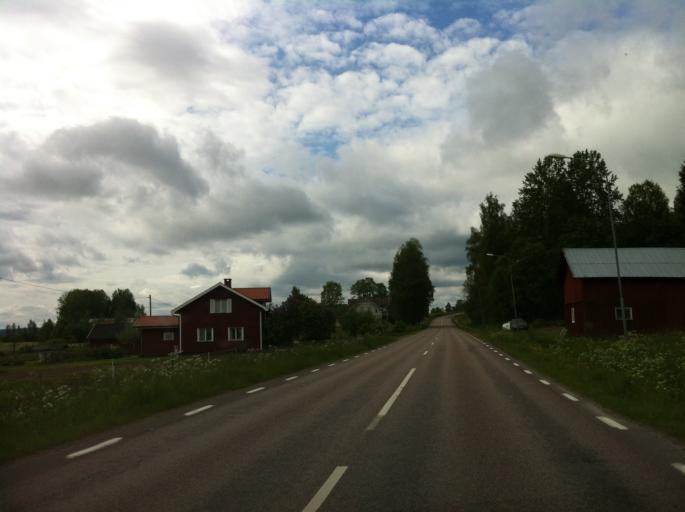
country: SE
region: Vaermland
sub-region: Sunne Kommun
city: Sunne
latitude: 59.8749
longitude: 13.1728
